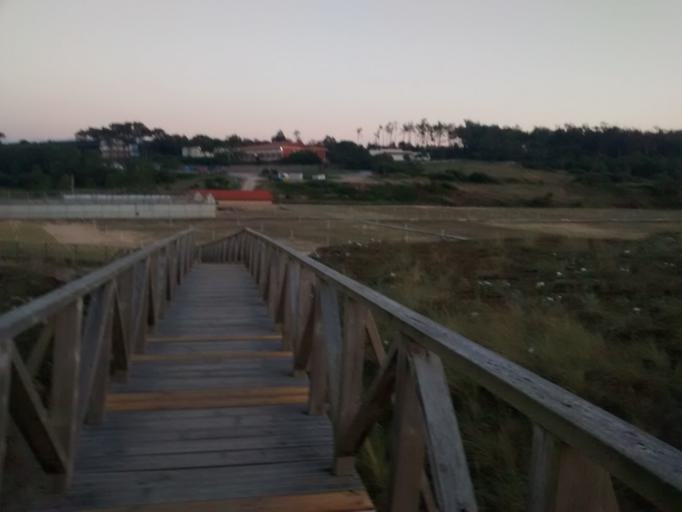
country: ES
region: Cantabria
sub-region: Provincia de Cantabria
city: Santander
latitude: 43.4612
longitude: -3.7272
